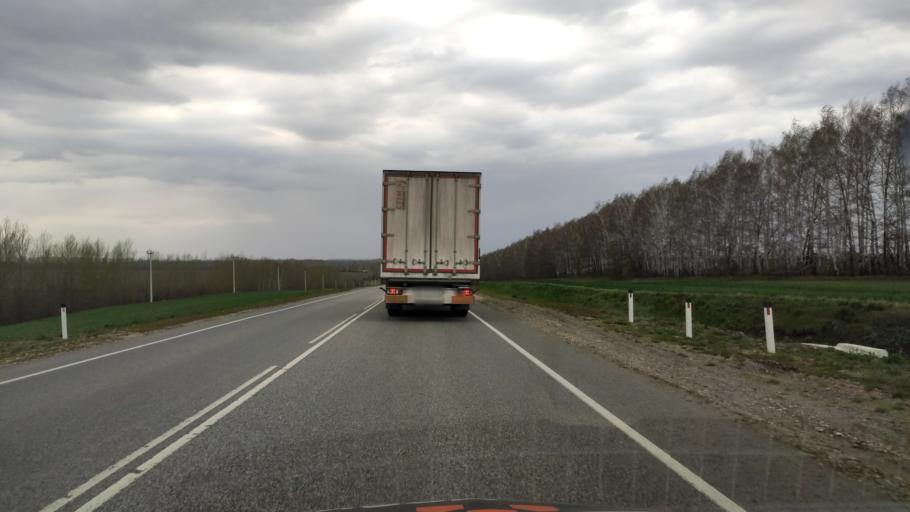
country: RU
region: Kursk
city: Gorshechnoye
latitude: 51.5490
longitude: 38.1333
